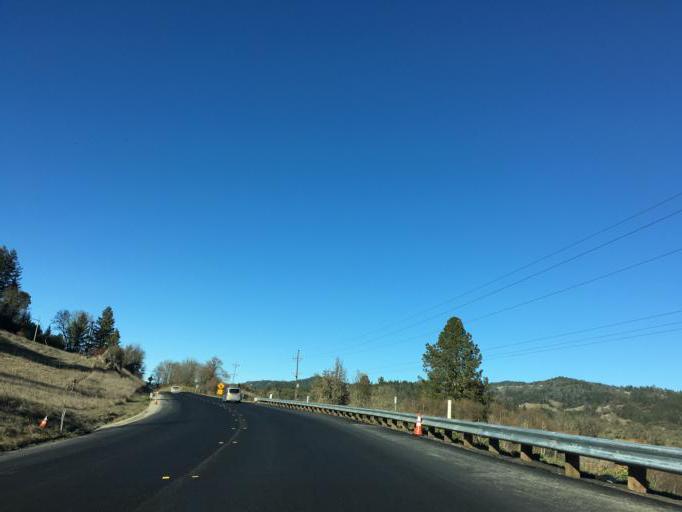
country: US
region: California
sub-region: Mendocino County
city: Laytonville
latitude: 39.6280
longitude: -123.4623
